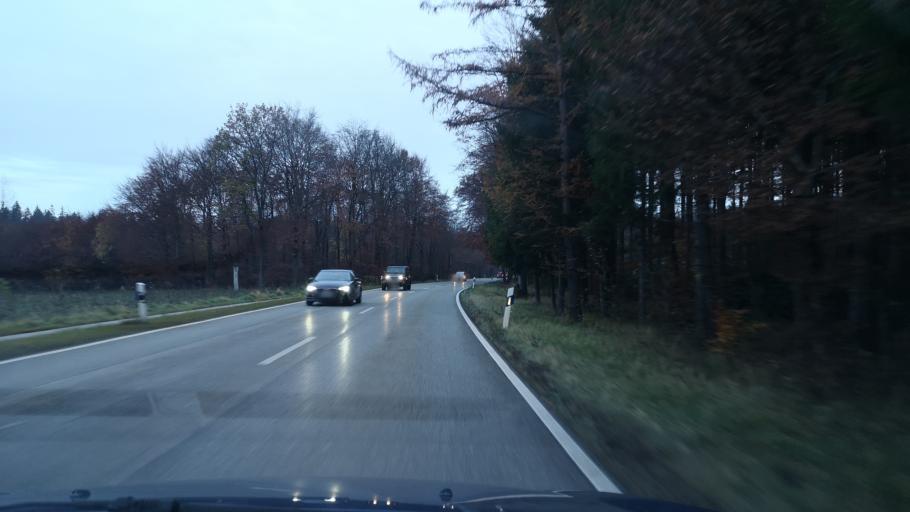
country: DE
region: Bavaria
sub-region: Upper Bavaria
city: Ebersberg
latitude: 48.1072
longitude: 11.9547
